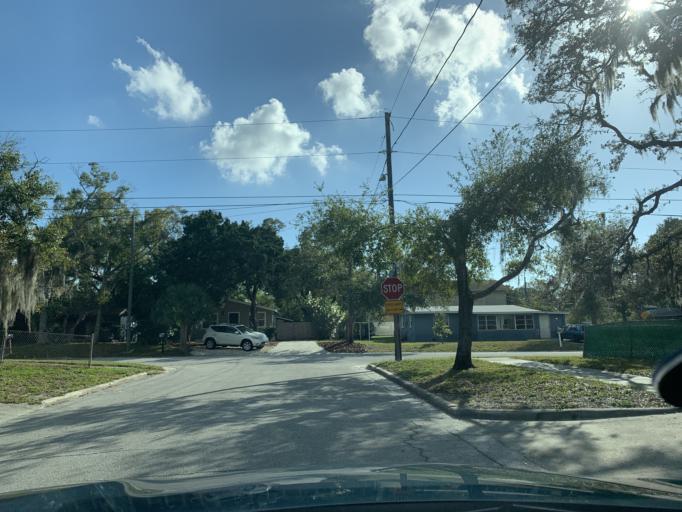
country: US
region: Florida
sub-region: Pinellas County
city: Belleair
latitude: 27.9465
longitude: -82.7892
